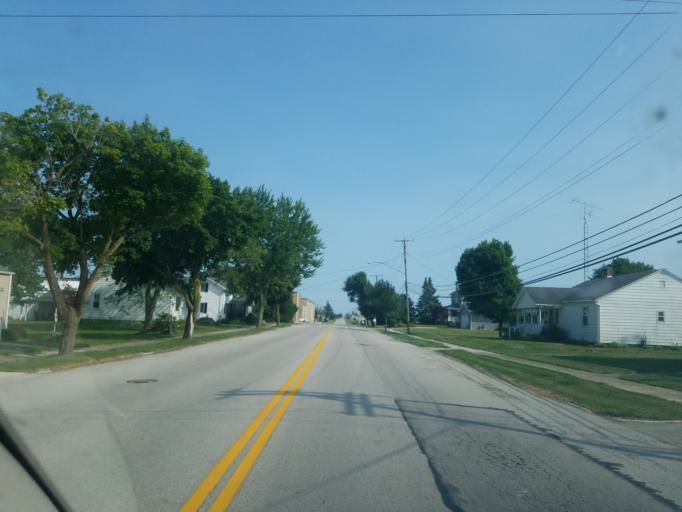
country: US
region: Ohio
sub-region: Wyandot County
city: Carey
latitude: 41.0499
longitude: -83.3169
